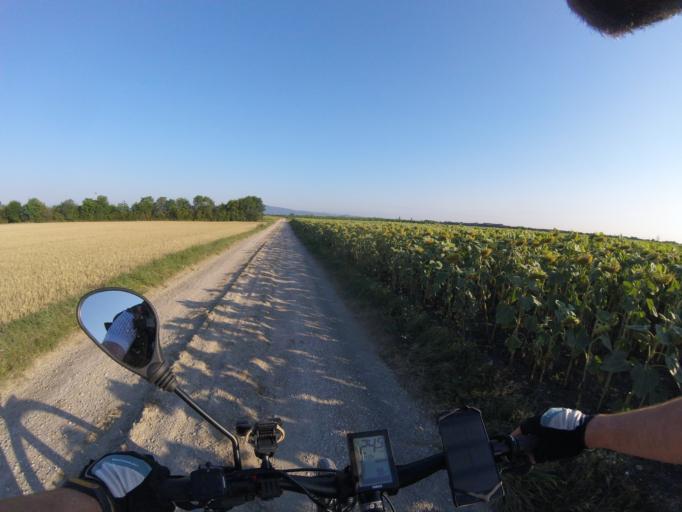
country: AT
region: Lower Austria
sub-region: Politischer Bezirk Baden
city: Trumau
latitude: 47.9801
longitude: 16.3579
